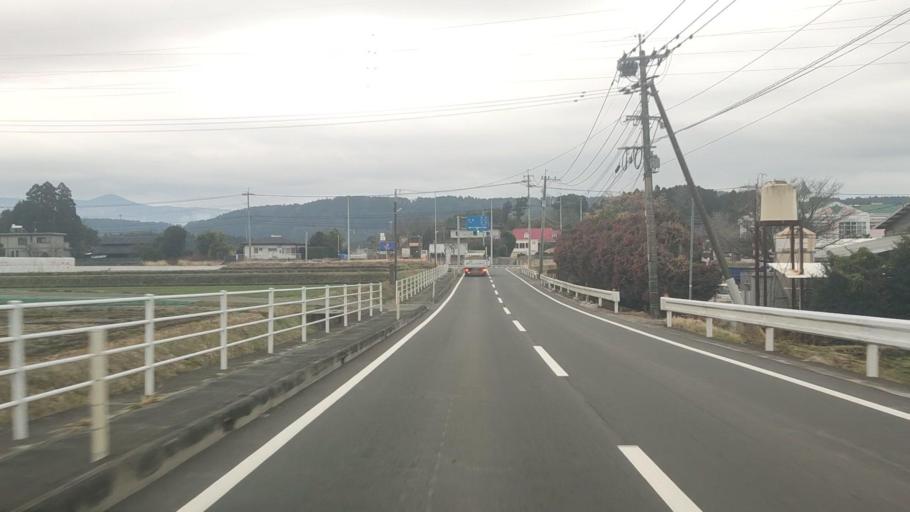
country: JP
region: Kumamoto
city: Ozu
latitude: 32.8664
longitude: 130.8906
